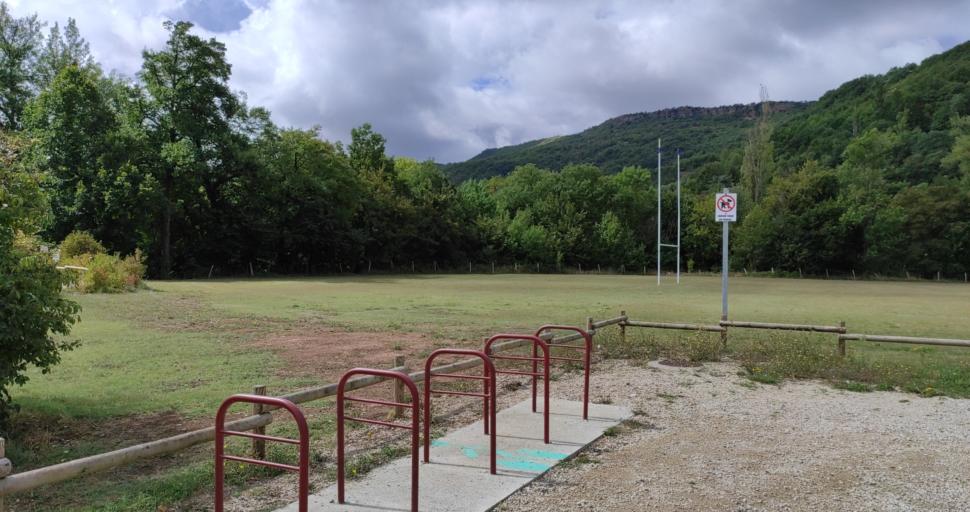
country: FR
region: Midi-Pyrenees
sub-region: Departement de l'Aveyron
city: Saint-Affrique
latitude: 43.9466
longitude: 2.8946
